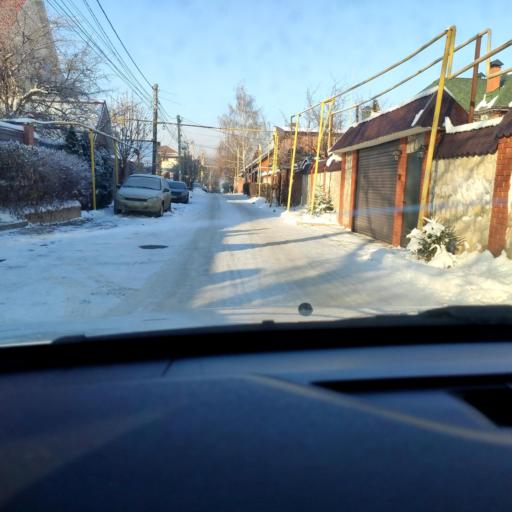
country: RU
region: Samara
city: Samara
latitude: 53.2716
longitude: 50.2038
